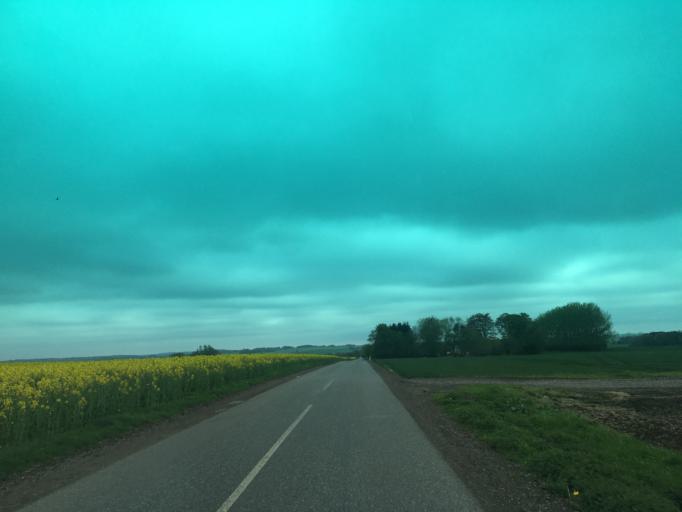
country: DK
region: Zealand
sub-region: Ringsted Kommune
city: Ringsted
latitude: 55.4268
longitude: 11.7124
